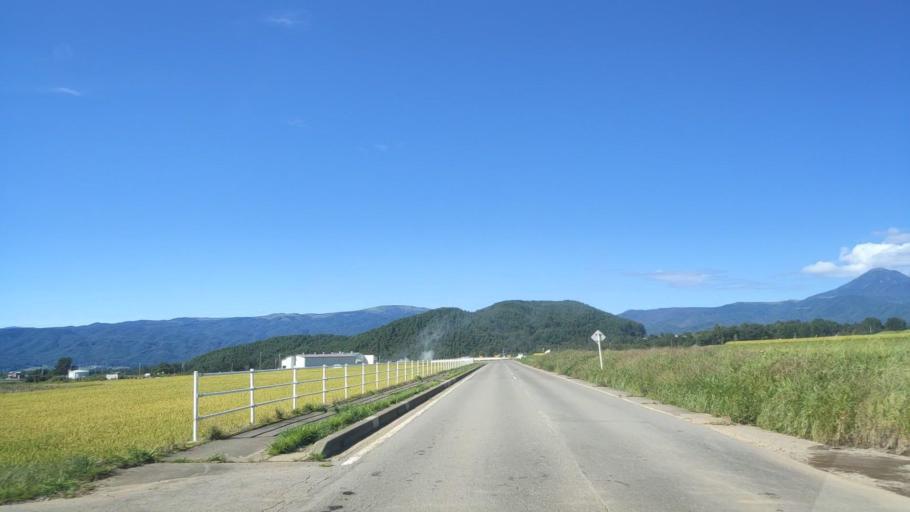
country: JP
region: Nagano
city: Chino
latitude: 35.9865
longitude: 138.2176
